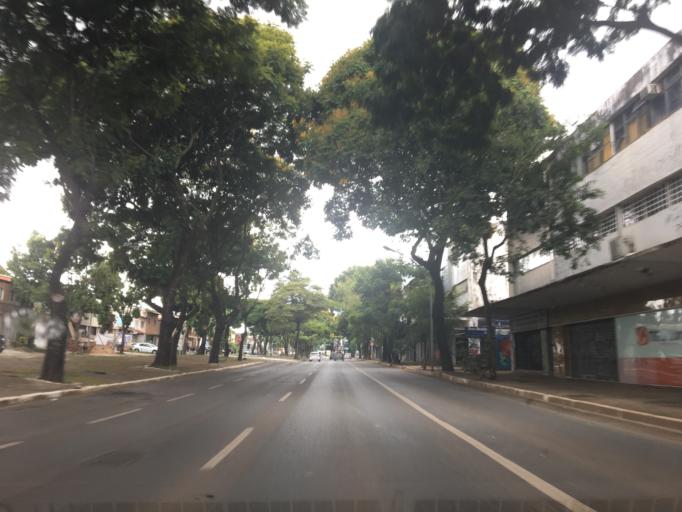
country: BR
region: Federal District
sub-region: Brasilia
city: Brasilia
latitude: -15.8114
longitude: -47.9048
